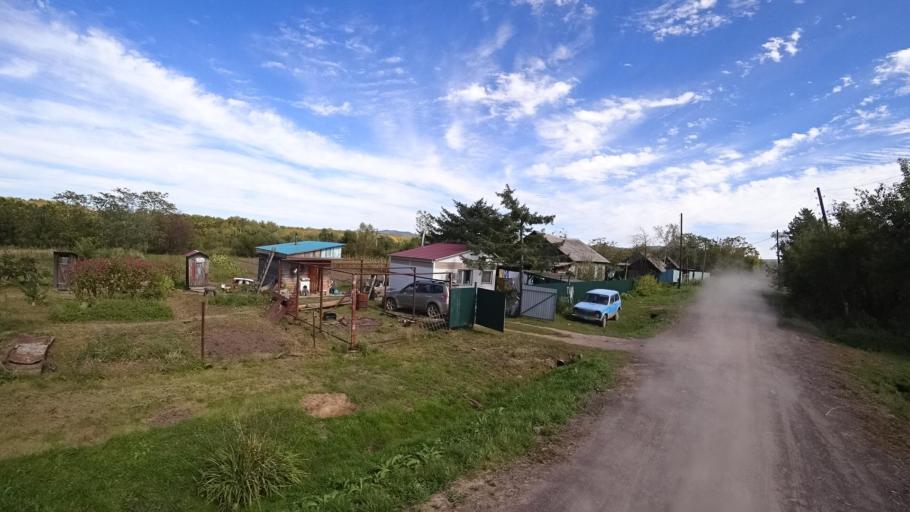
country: RU
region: Primorskiy
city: Yakovlevka
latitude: 44.4361
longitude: 133.5635
